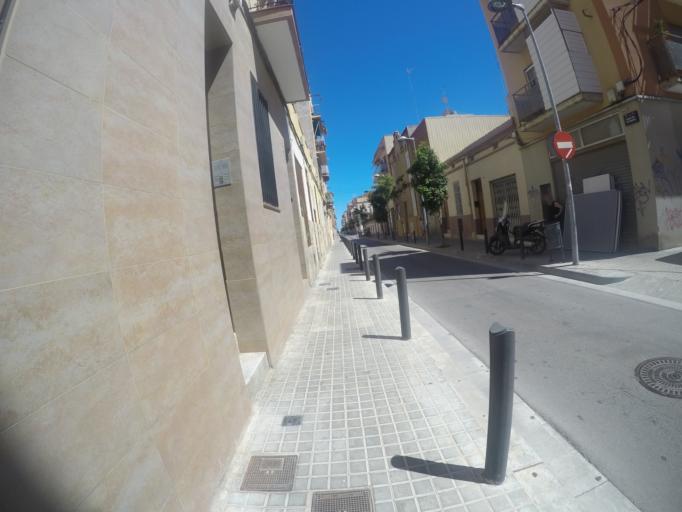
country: ES
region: Catalonia
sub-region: Provincia de Barcelona
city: Badalona
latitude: 41.4425
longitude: 2.2401
